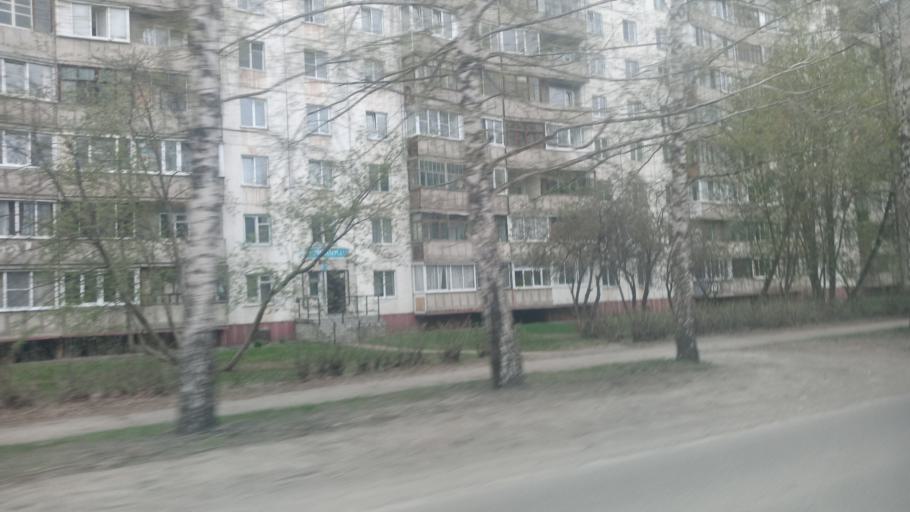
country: RU
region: Altai Krai
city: Yuzhnyy
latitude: 53.2501
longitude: 83.6885
